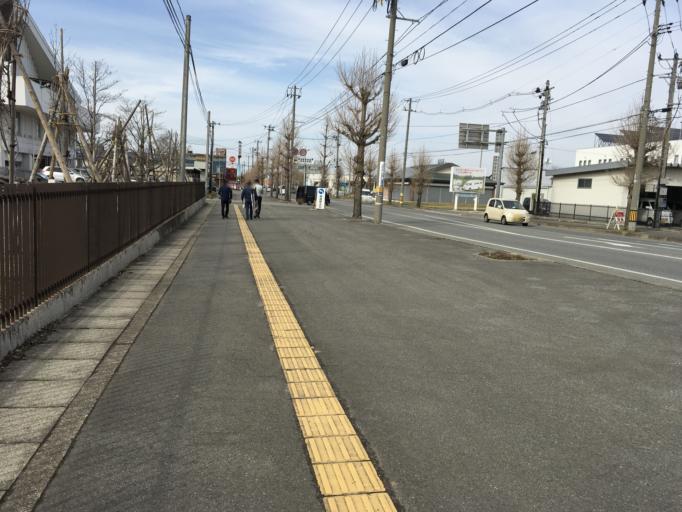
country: JP
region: Yamagata
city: Yonezawa
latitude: 37.9215
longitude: 140.1174
